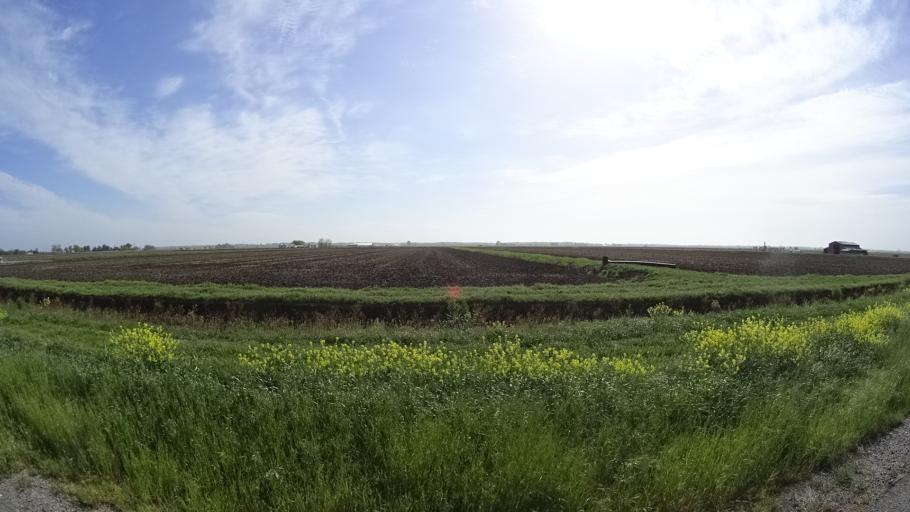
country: US
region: California
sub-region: Glenn County
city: Willows
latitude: 39.5701
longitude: -122.0464
